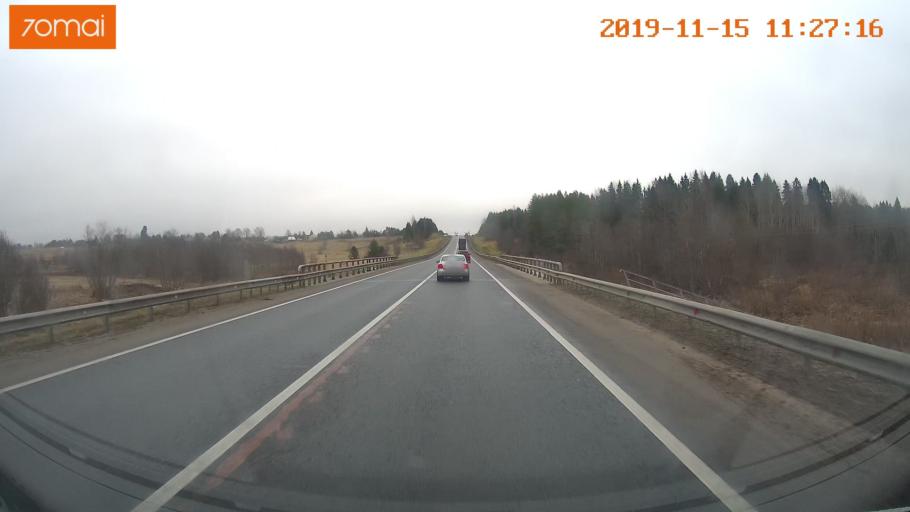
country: RU
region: Vologda
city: Molochnoye
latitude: 59.1693
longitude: 39.4633
